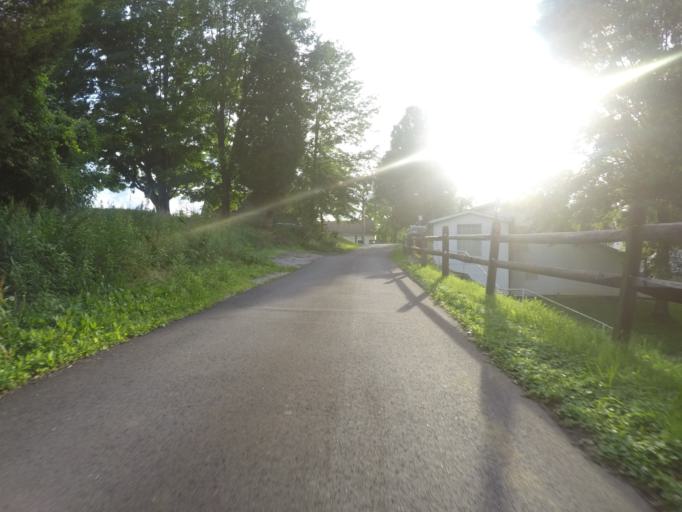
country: US
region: West Virginia
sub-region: Cabell County
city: Pea Ridge
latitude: 38.4067
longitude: -82.3624
